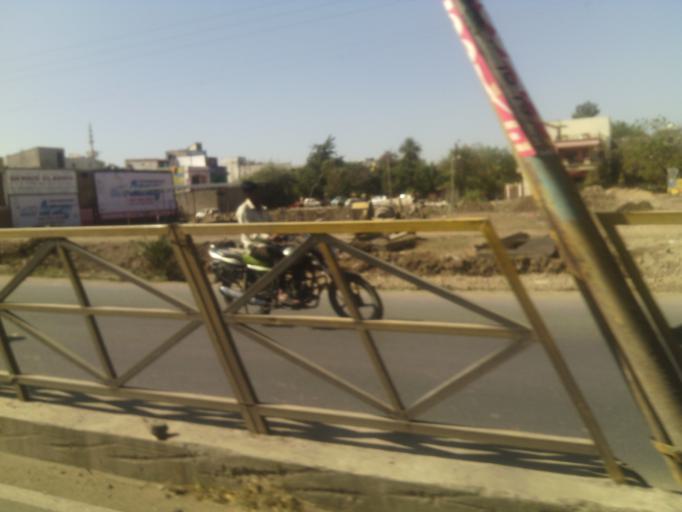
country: IN
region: Madhya Pradesh
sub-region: Dewas
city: Dewas
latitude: 22.9581
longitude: 76.0423
